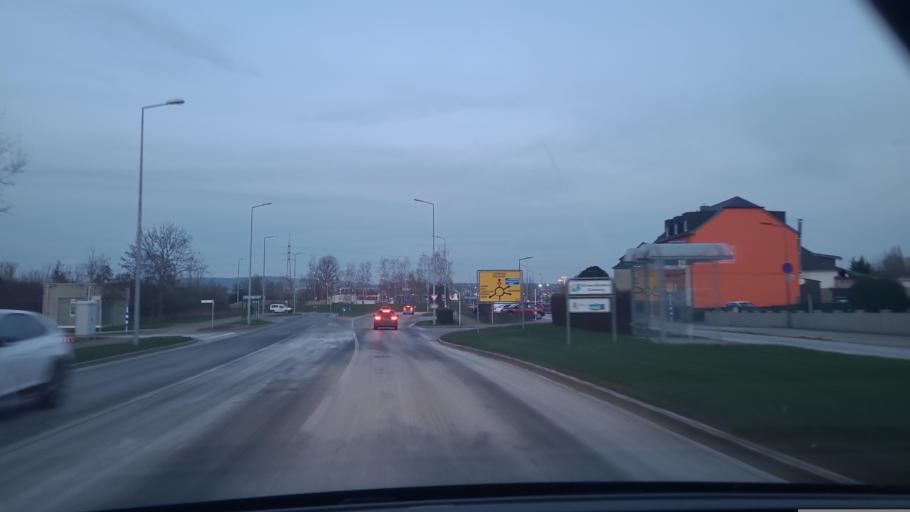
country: LU
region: Luxembourg
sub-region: Canton d'Esch-sur-Alzette
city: Petange
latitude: 49.5597
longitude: 5.8936
